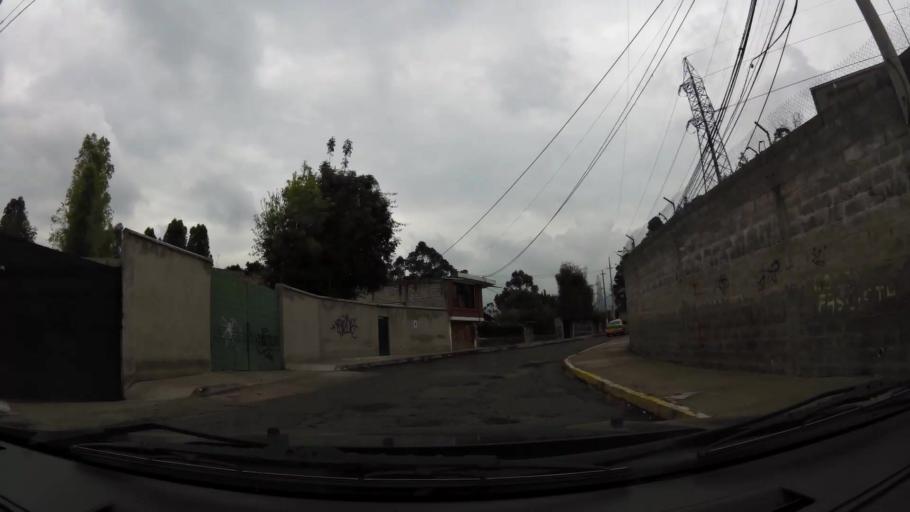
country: EC
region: Pichincha
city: Sangolqui
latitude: -0.3005
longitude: -78.4667
